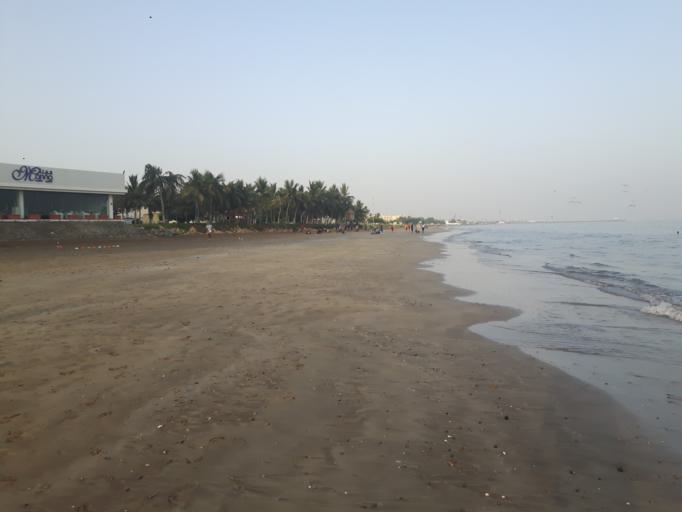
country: OM
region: Muhafazat Masqat
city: Bawshar
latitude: 23.6132
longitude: 58.4529
